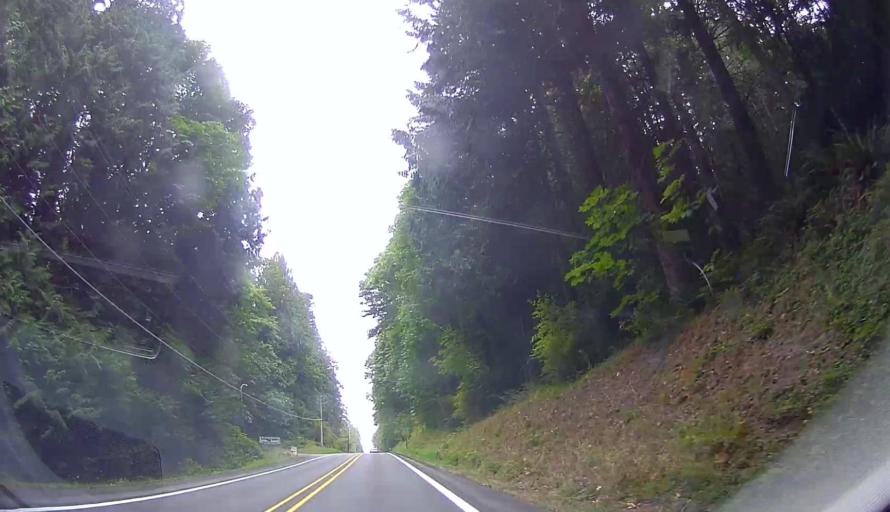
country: US
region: Washington
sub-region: Snohomish County
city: Warm Beach
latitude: 48.1289
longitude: -122.3558
